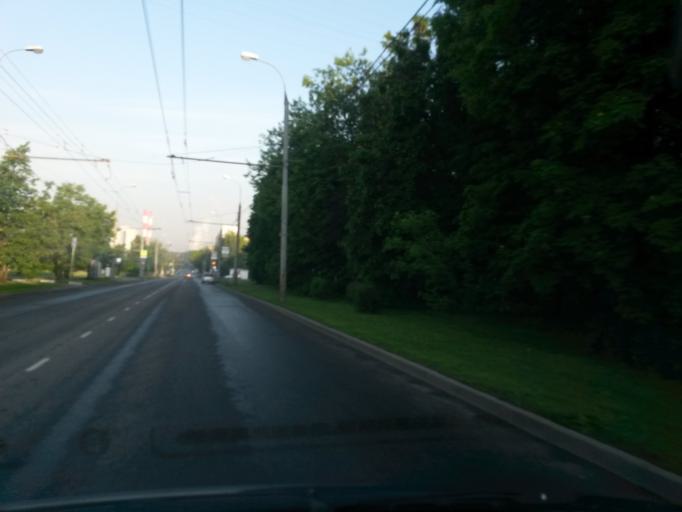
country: RU
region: Moscow
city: Gol'yanovo
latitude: 55.8234
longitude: 37.8140
